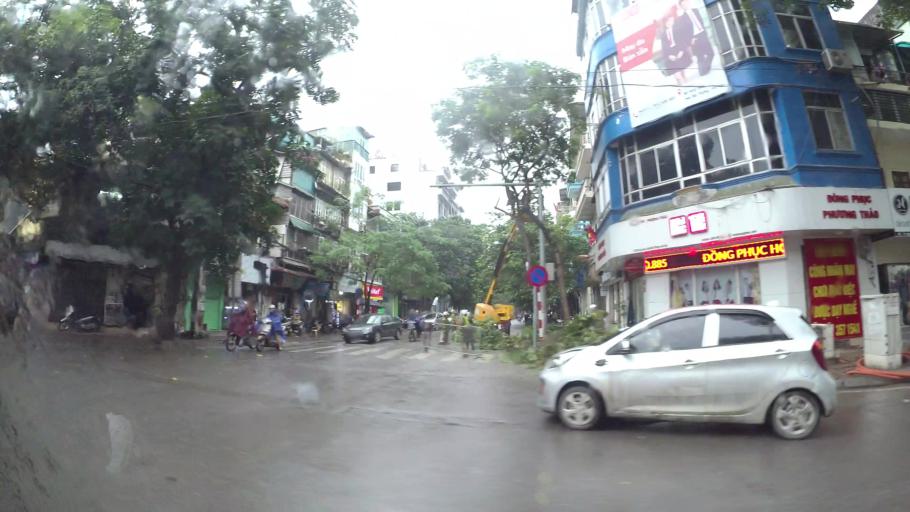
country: VN
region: Ha Noi
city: Hai BaTrung
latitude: 21.0153
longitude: 105.8531
